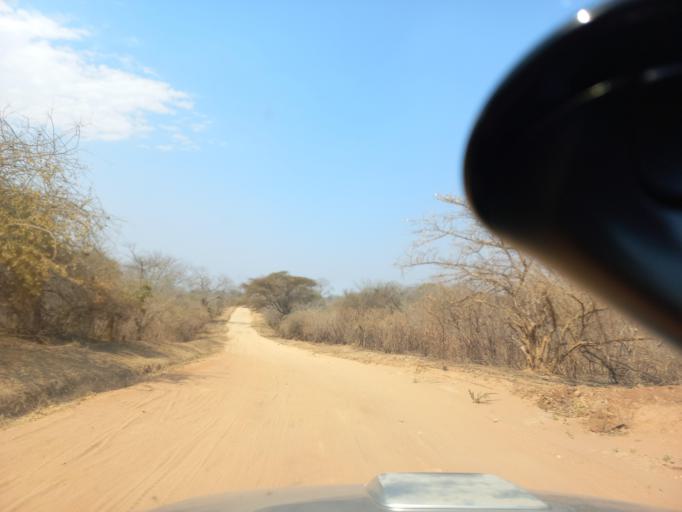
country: ZW
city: Chirundu
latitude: -15.9257
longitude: 28.8857
